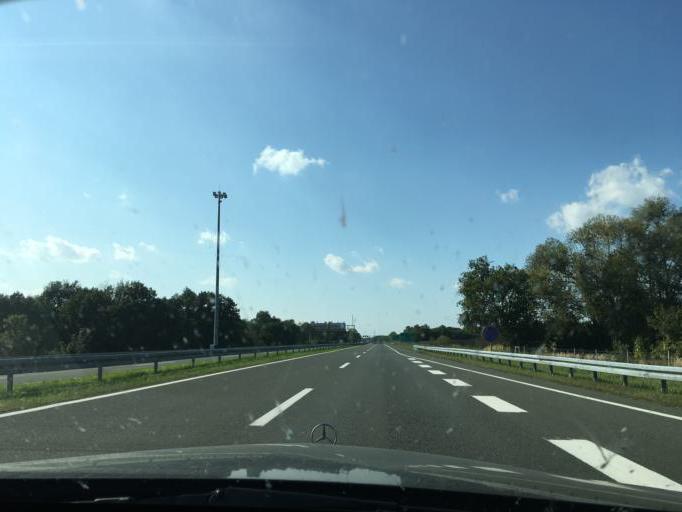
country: HR
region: Medimurska
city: Hodosan
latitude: 46.4093
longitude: 16.6648
